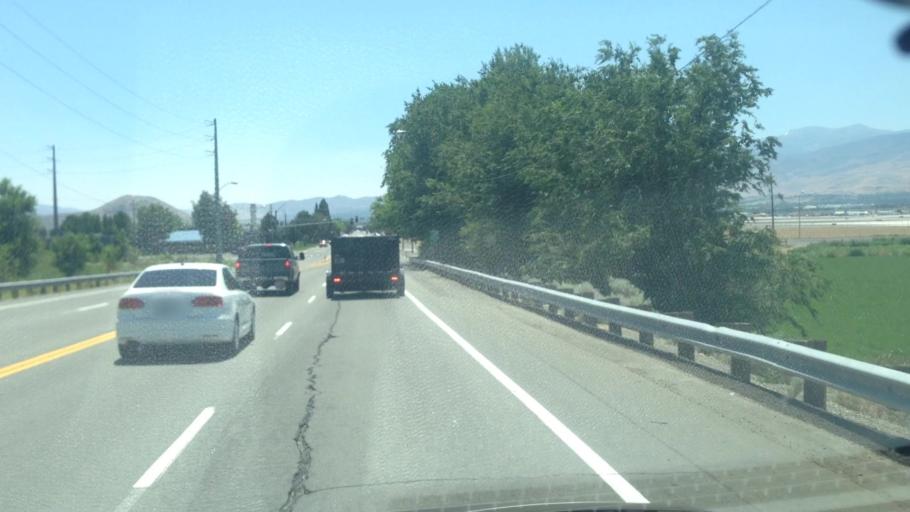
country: US
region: Nevada
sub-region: Washoe County
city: Sparks
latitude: 39.5178
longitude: -119.7614
